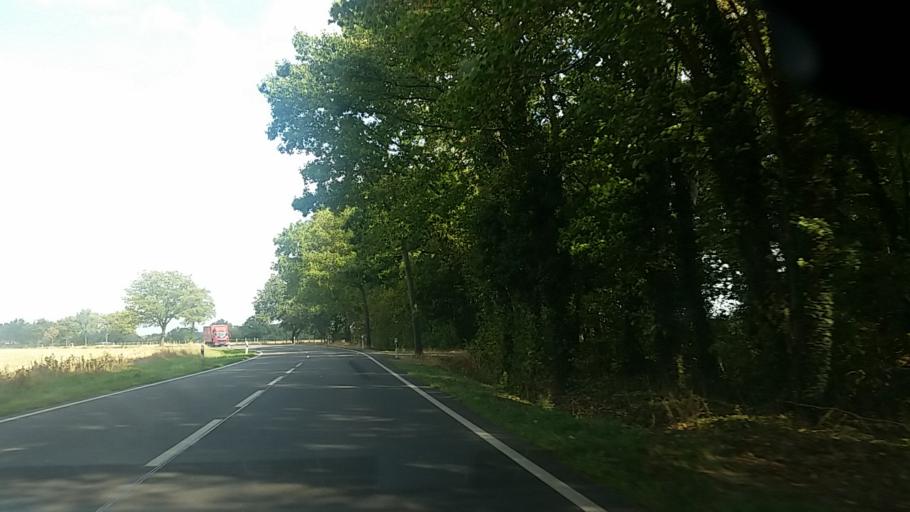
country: DE
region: Saxony-Anhalt
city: Jubar
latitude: 52.6616
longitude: 10.8524
